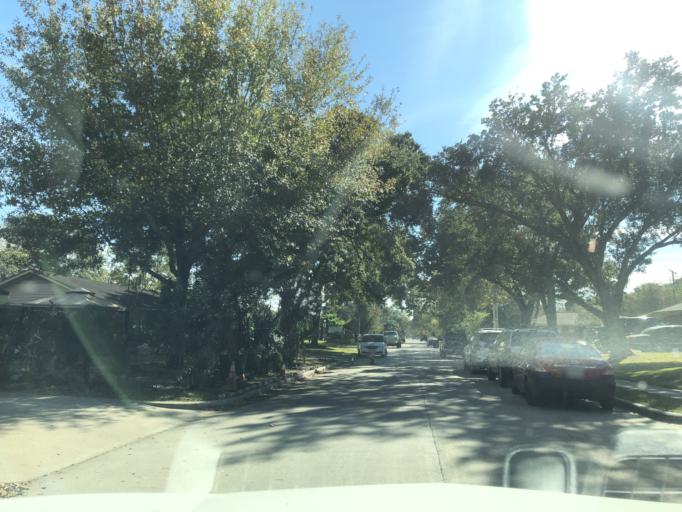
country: US
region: Texas
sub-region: Harris County
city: Bellaire
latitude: 29.6829
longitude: -95.5109
